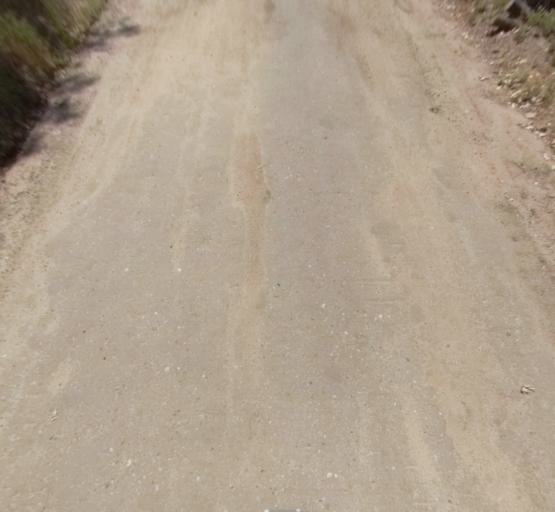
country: US
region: California
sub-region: Fresno County
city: Auberry
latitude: 37.2356
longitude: -119.4616
